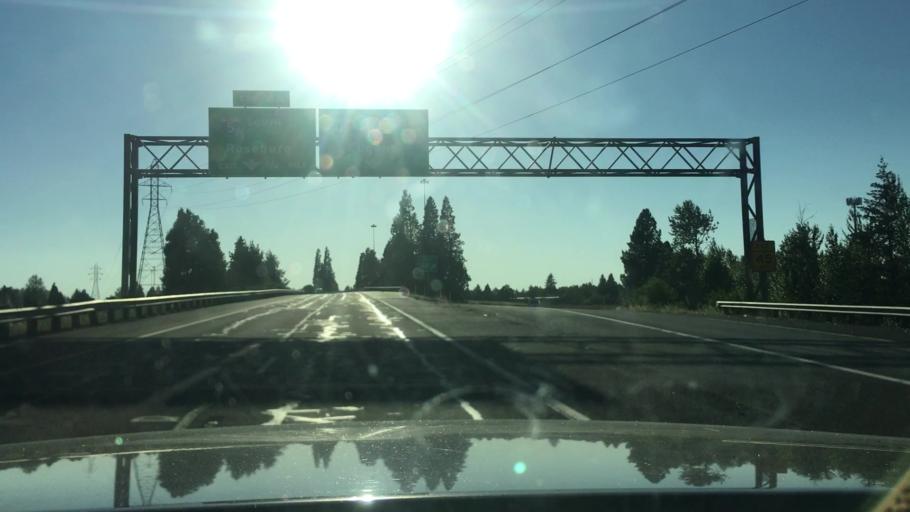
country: US
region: Oregon
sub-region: Lane County
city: Springfield
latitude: 44.0634
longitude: -123.0437
